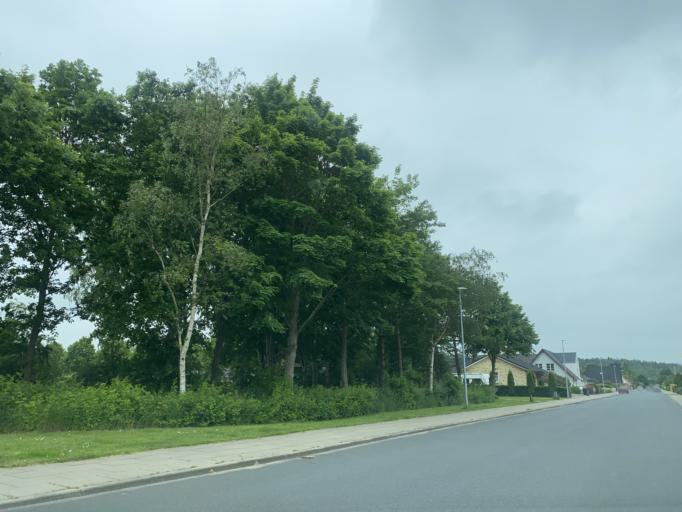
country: DK
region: Central Jutland
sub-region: Viborg Kommune
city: Bjerringbro
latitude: 56.3669
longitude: 9.6585
